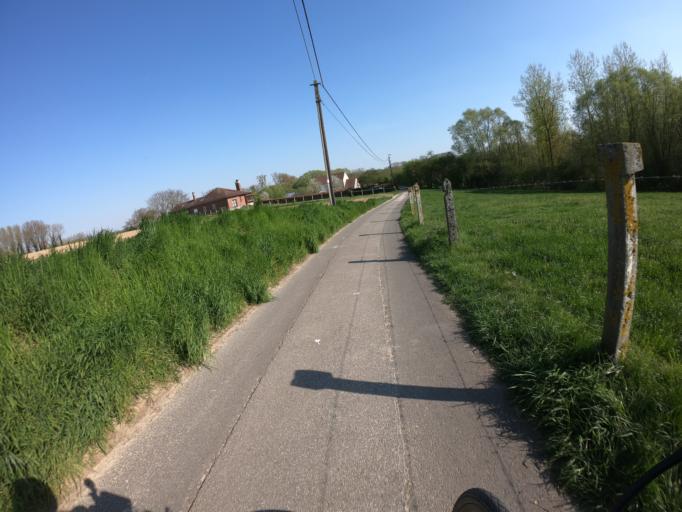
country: BE
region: Flanders
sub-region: Provincie Oost-Vlaanderen
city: Ninove
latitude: 50.8304
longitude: 3.9998
